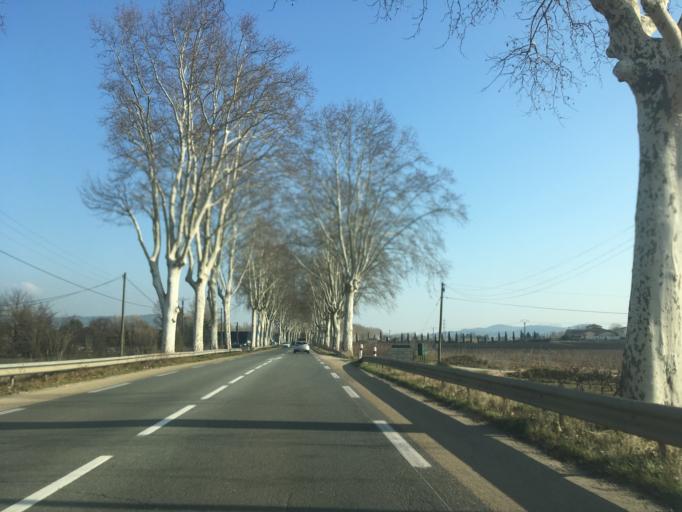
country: FR
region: Provence-Alpes-Cote d'Azur
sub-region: Departement du Var
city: Vidauban
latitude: 43.4403
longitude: 6.4541
